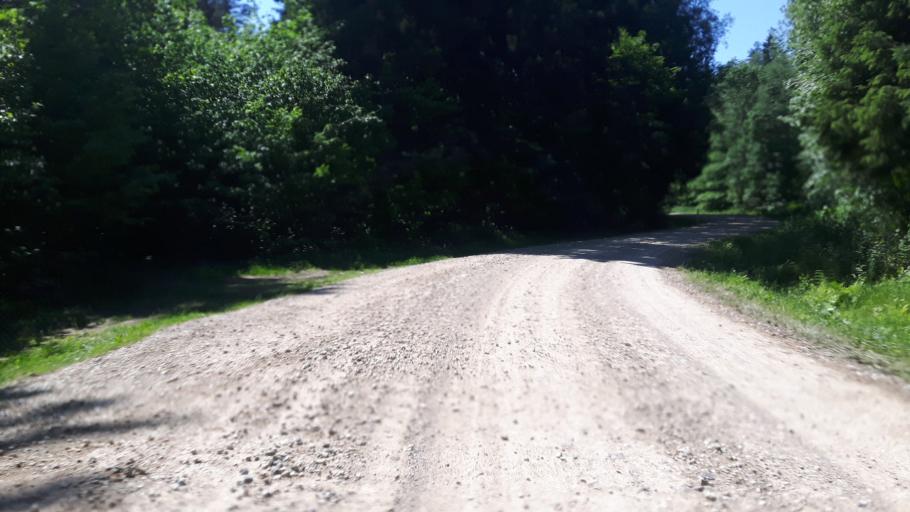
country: EE
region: Paernumaa
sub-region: Tootsi vald
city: Tootsi
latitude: 58.5069
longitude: 24.9075
